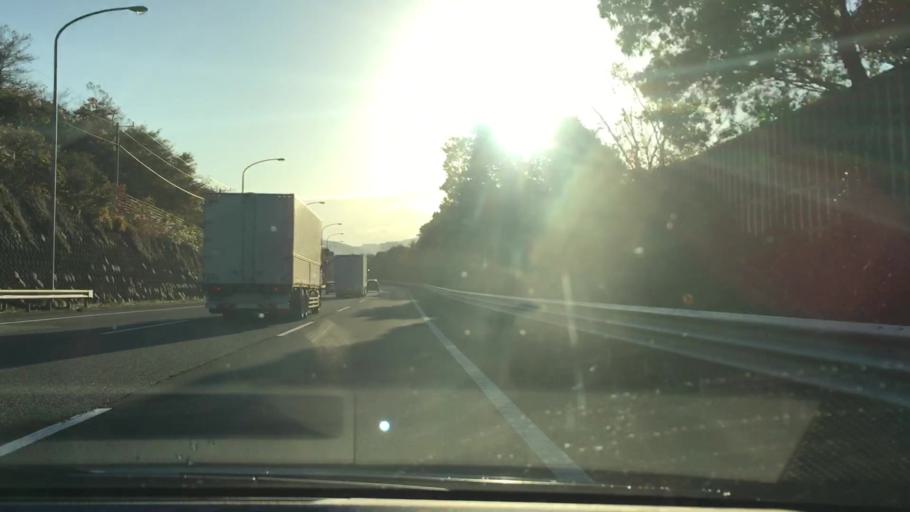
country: JP
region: Kanagawa
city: Hadano
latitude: 35.3529
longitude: 139.1253
